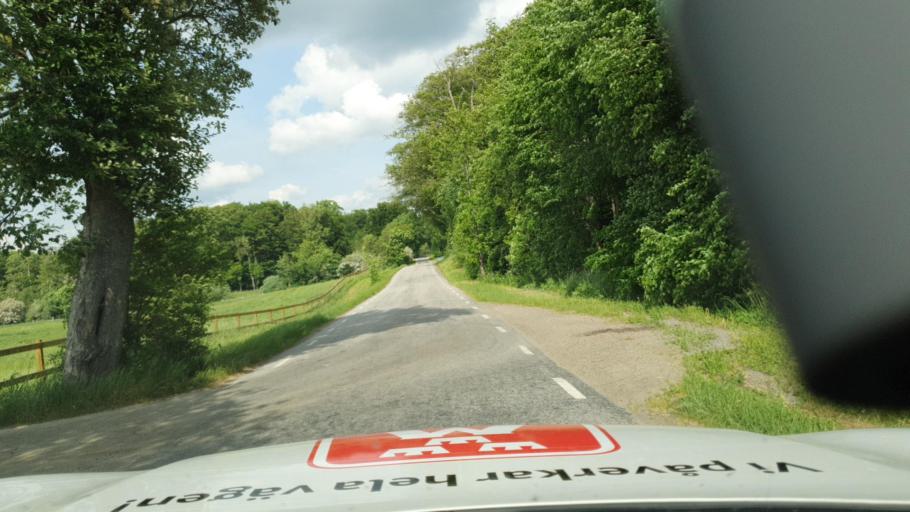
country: SE
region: Skane
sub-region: Skurups Kommun
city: Skurup
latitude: 55.5095
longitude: 13.4964
